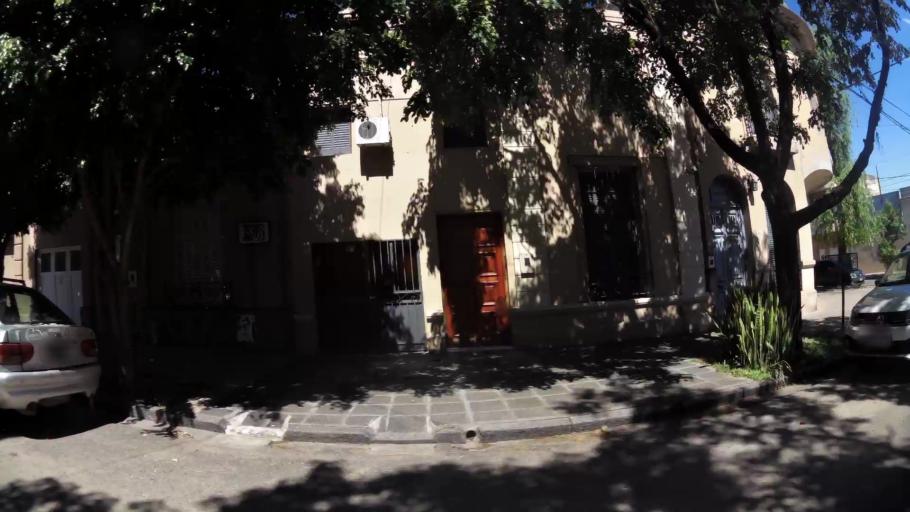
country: AR
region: Santa Fe
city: Santa Fe de la Vera Cruz
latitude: -31.6424
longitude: -60.6891
